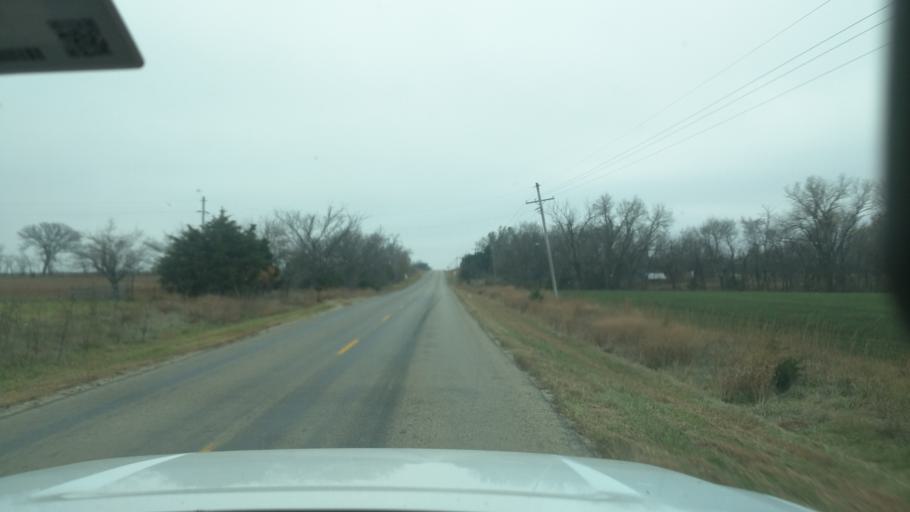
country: US
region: Kansas
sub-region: Lyon County
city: Emporia
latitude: 38.5595
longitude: -96.2612
